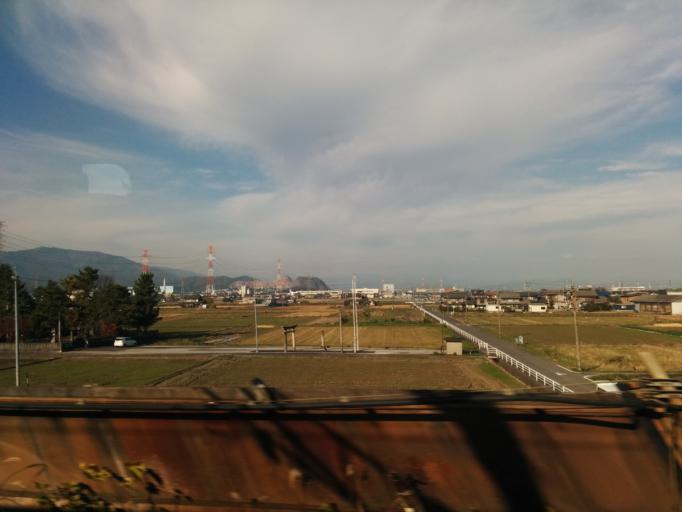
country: JP
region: Gifu
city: Ogaki
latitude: 35.3488
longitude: 136.5886
